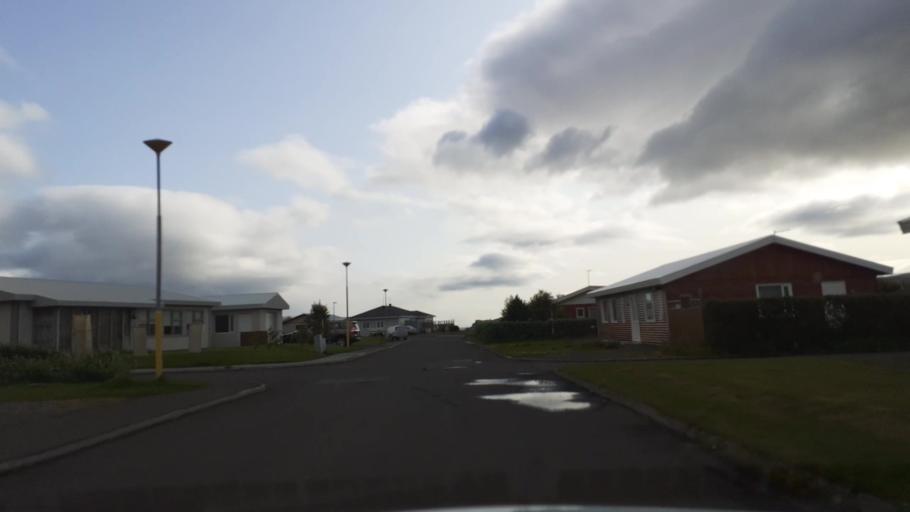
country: IS
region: East
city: Neskaupstadur
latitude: 65.1489
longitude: -13.6599
